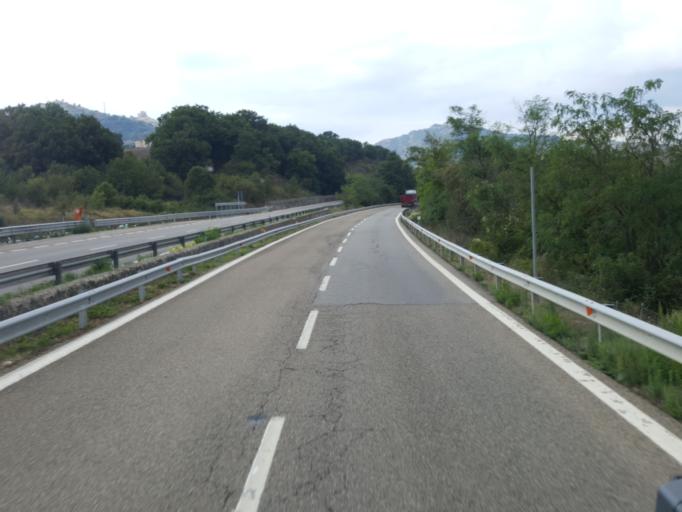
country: IT
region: Basilicate
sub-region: Provincia di Potenza
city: Brindisi Montagna
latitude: 40.6061
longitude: 15.9690
